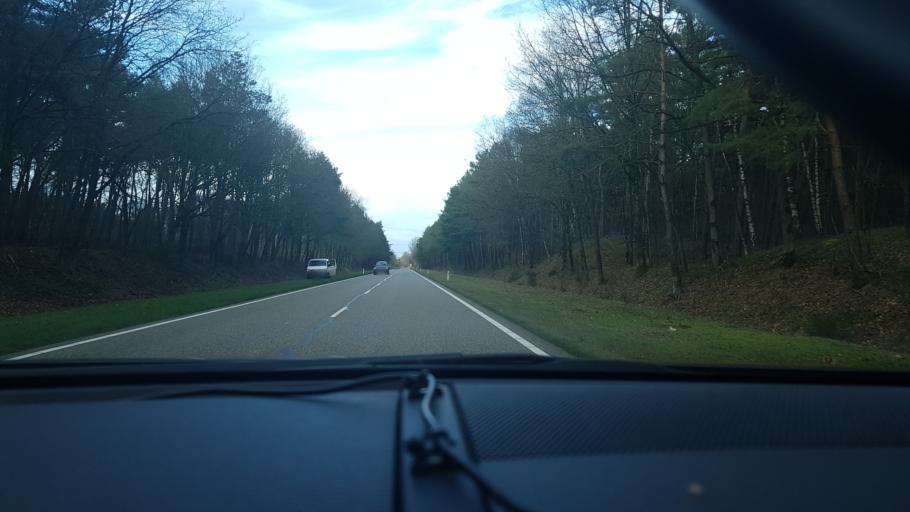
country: NL
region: Limburg
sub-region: Gemeente Peel en Maas
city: Maasbree
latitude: 51.3218
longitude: 6.0445
